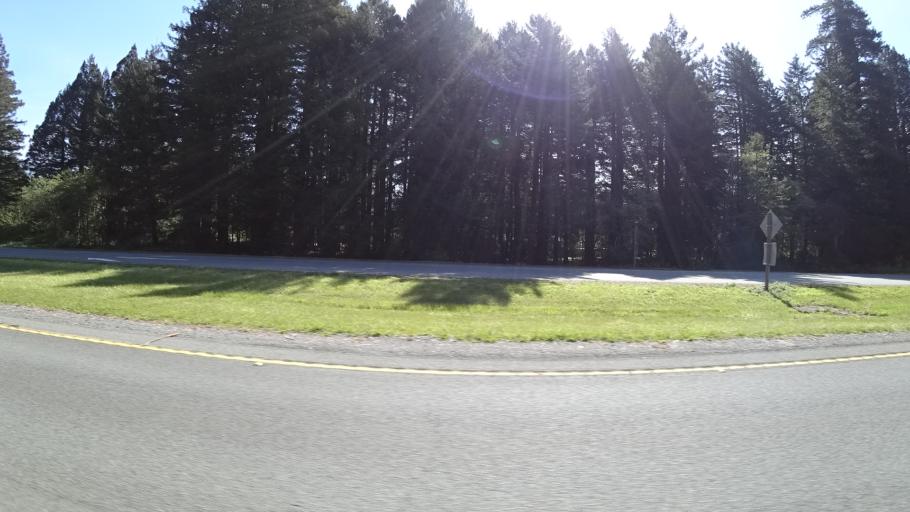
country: US
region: California
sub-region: Del Norte County
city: Bertsch-Oceanview
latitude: 41.8088
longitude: -124.1475
